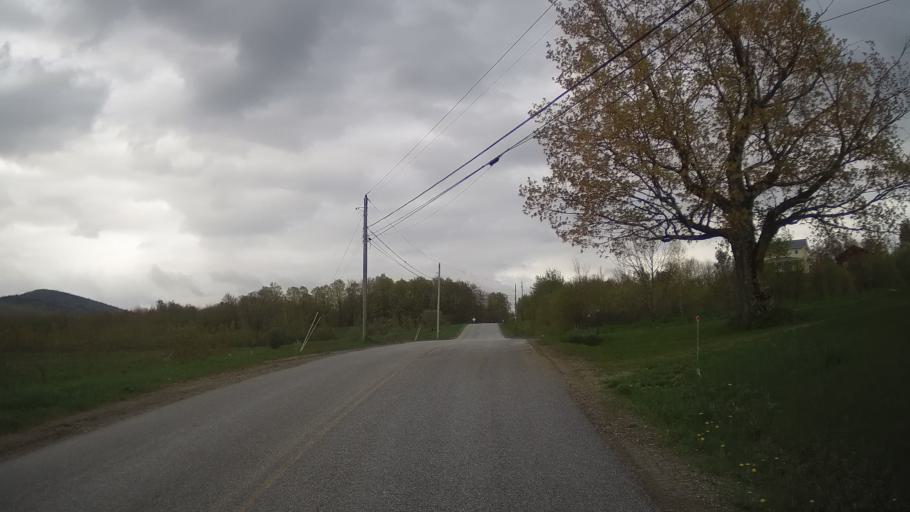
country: US
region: Vermont
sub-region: Franklin County
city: Richford
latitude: 44.9823
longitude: -72.6609
